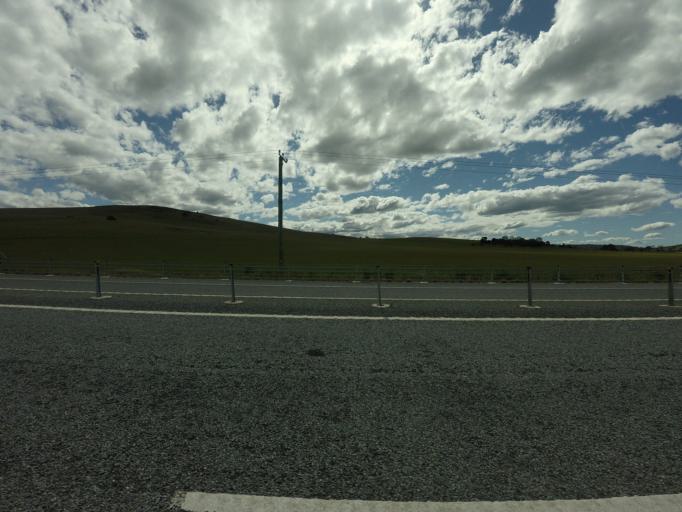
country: AU
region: Tasmania
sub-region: Northern Midlands
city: Evandale
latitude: -42.1046
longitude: 147.4488
